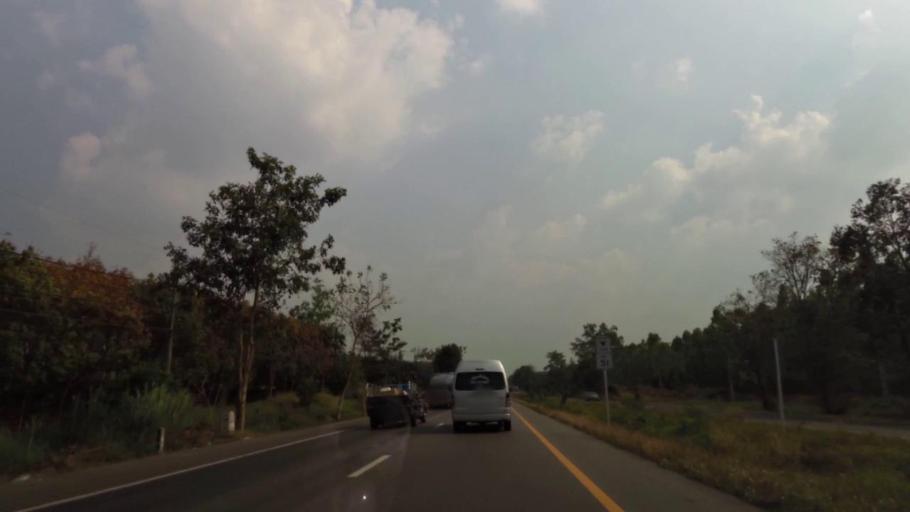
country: TH
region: Chon Buri
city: Nong Yai
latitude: 13.1247
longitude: 101.3618
